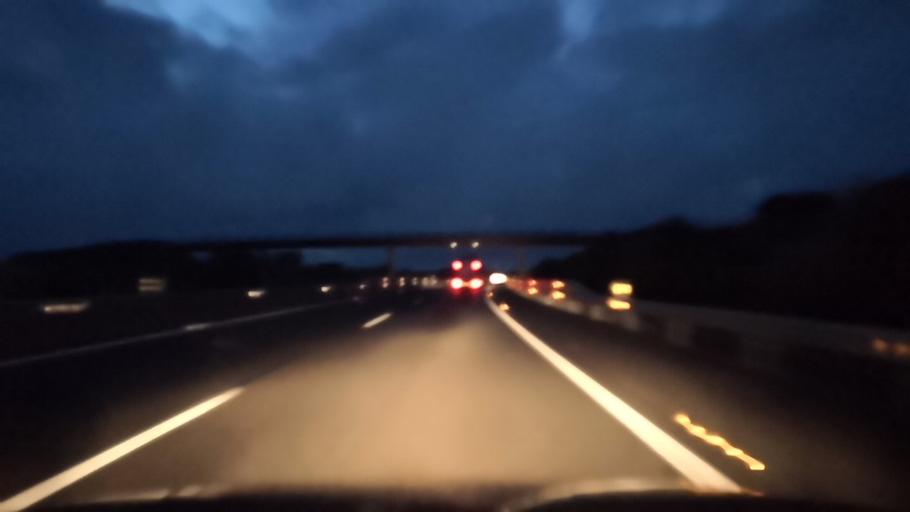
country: ES
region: Extremadura
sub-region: Provincia de Caceres
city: Caceres
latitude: 39.4784
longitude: -6.4338
